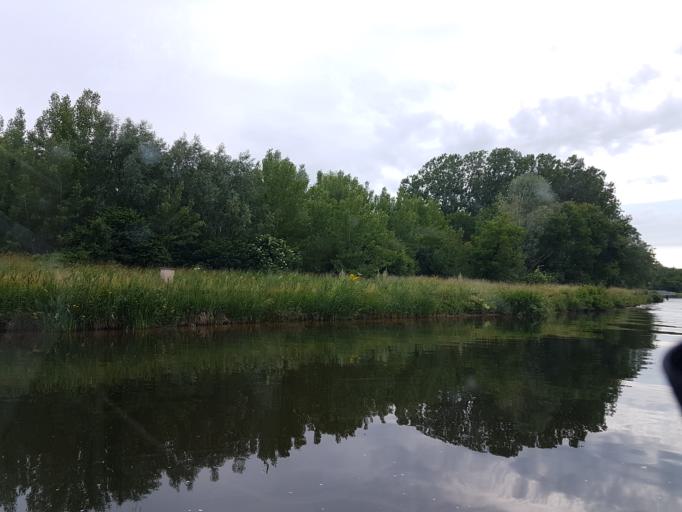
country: FR
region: Bourgogne
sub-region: Departement de l'Yonne
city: Auxerre
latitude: 47.8179
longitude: 3.5800
